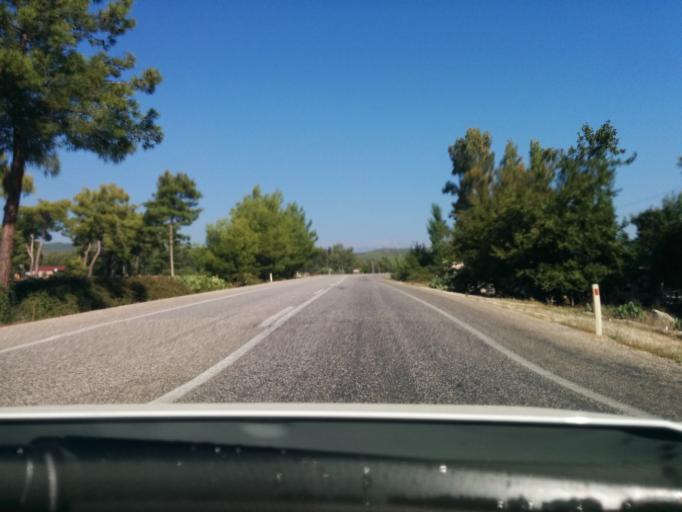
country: TR
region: Mugla
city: Kemer
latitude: 36.5837
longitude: 29.3506
